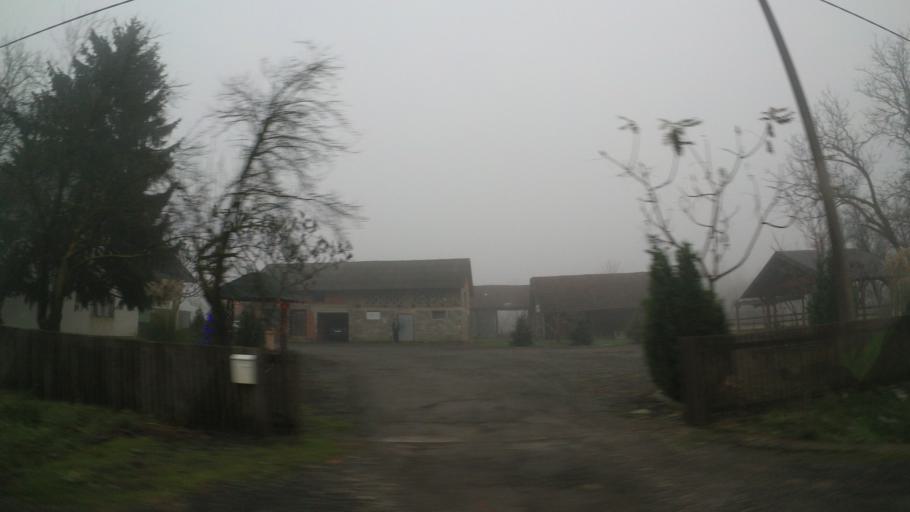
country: HR
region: Sisacko-Moslavacka
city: Petrinja
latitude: 45.4608
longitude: 16.2527
